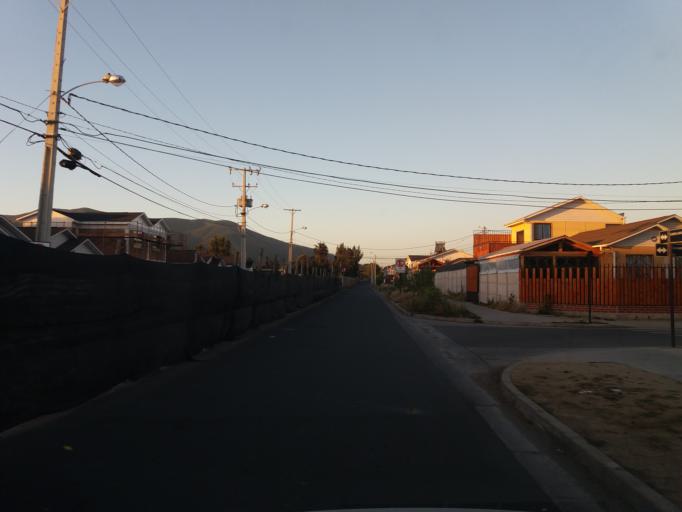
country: CL
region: Valparaiso
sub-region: Provincia de Quillota
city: Quillota
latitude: -32.8875
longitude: -71.2557
